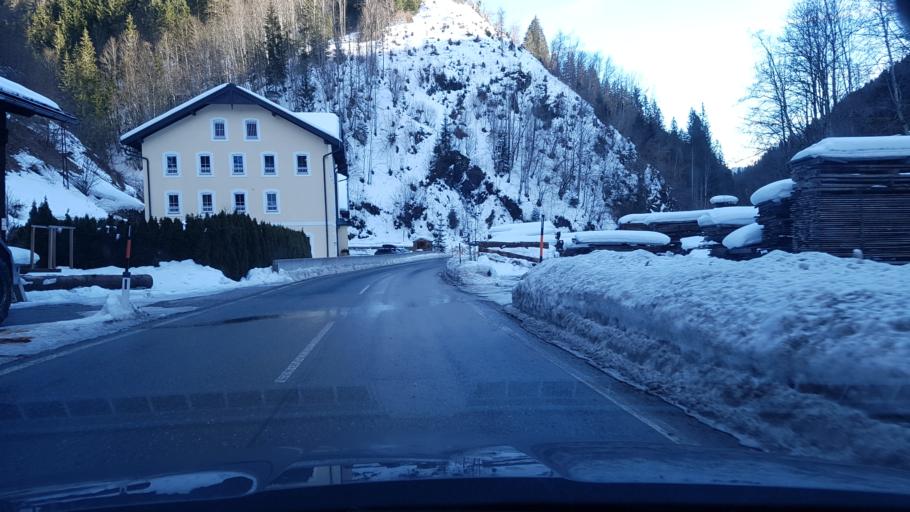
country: AT
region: Salzburg
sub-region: Politischer Bezirk Zell am See
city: Dienten am Hochkonig
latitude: 47.3368
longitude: 13.0172
